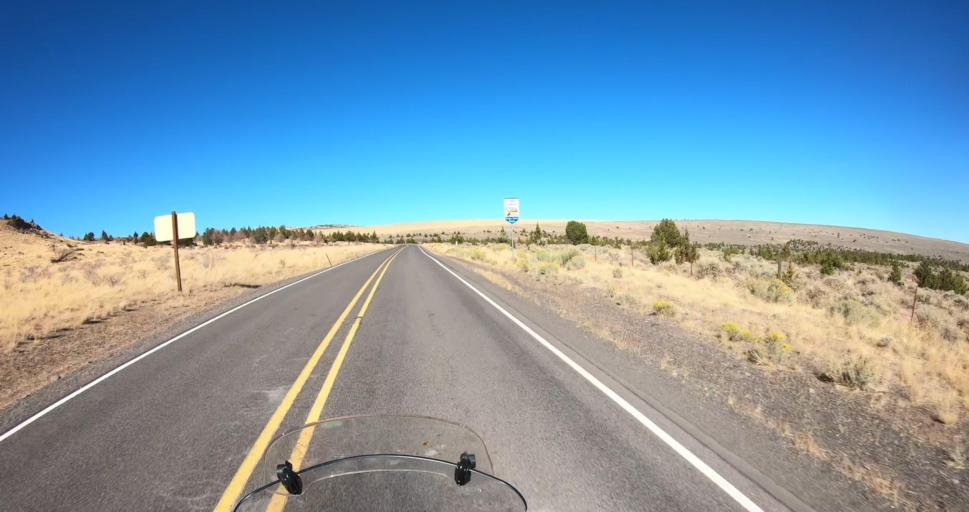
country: US
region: Oregon
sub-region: Lake County
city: Lakeview
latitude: 43.0069
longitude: -120.7749
